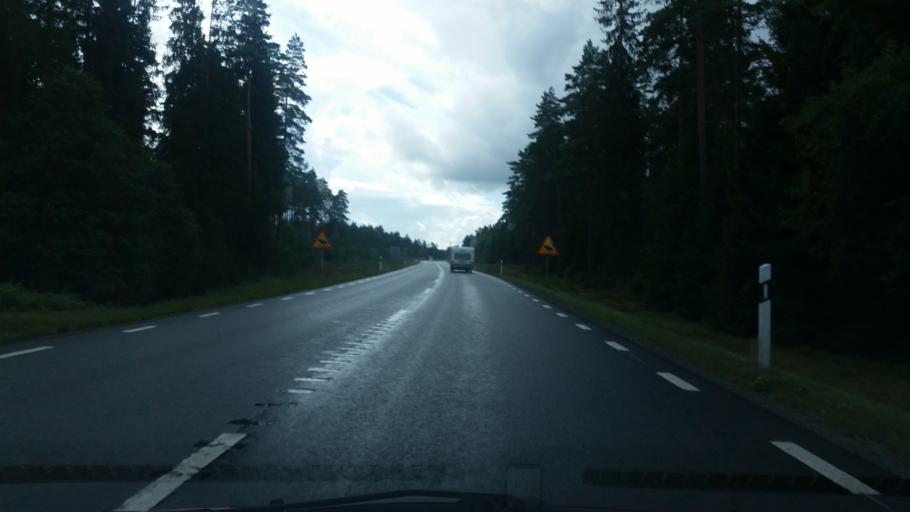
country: SE
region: Joenkoeping
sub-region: Gislaveds Kommun
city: Gislaved
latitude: 57.3539
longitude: 13.5580
